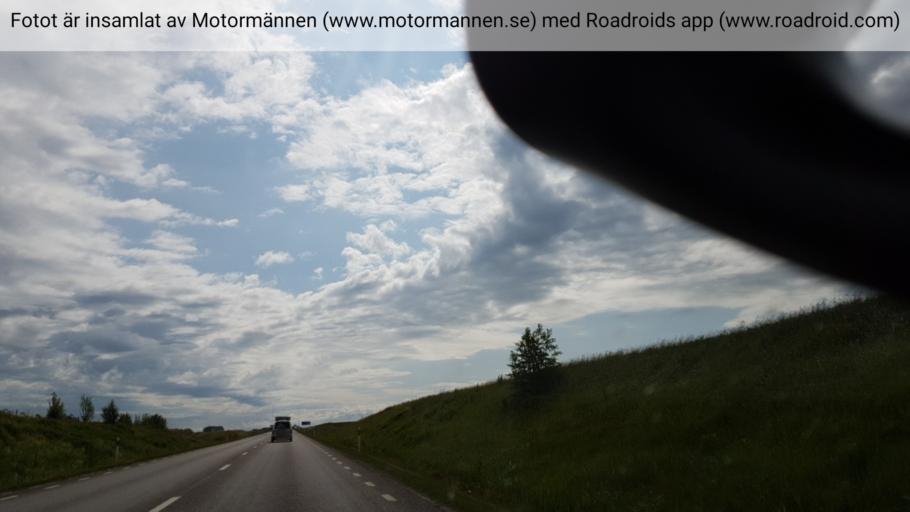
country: SE
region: Vaestra Goetaland
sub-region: Vara Kommun
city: Vara
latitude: 58.2976
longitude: 12.9404
